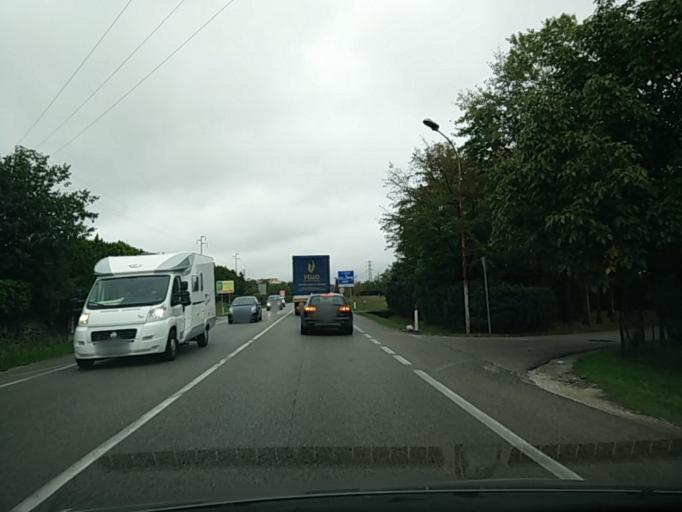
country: IT
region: Veneto
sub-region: Provincia di Treviso
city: Castelfranco Veneto
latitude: 45.6856
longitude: 11.9511
